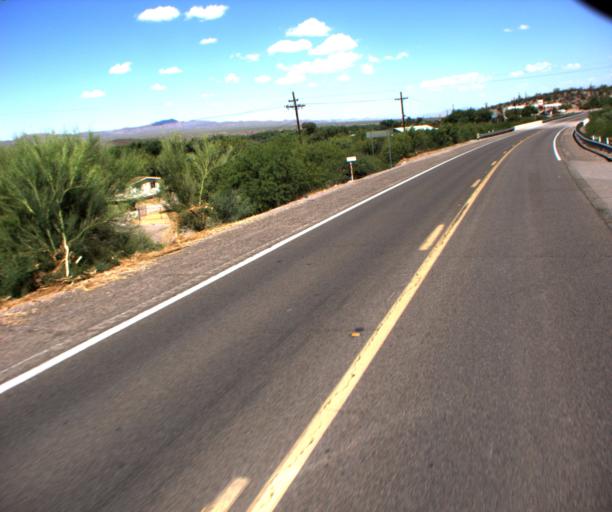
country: US
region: Arizona
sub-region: Pinal County
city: Kearny
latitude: 32.9305
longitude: -110.7331
